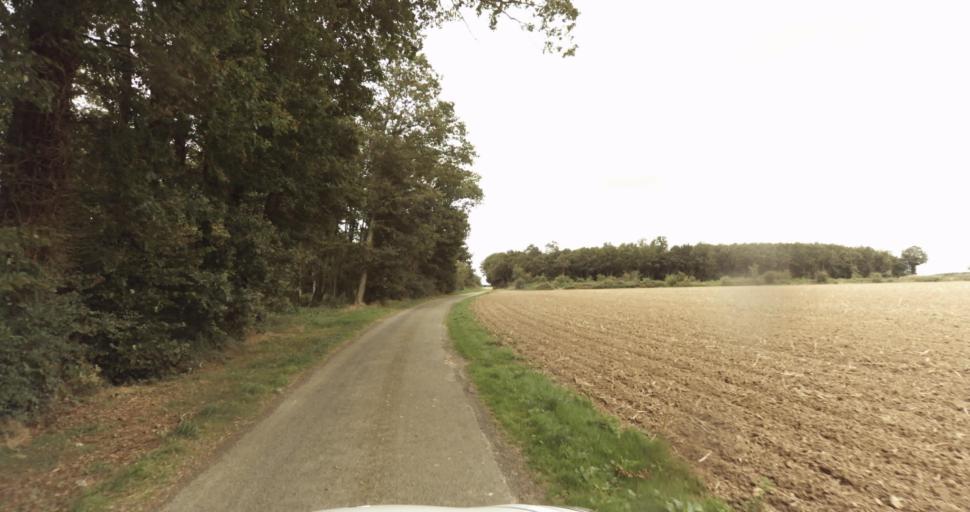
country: FR
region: Haute-Normandie
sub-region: Departement de l'Eure
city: Nonancourt
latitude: 48.8142
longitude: 1.1622
